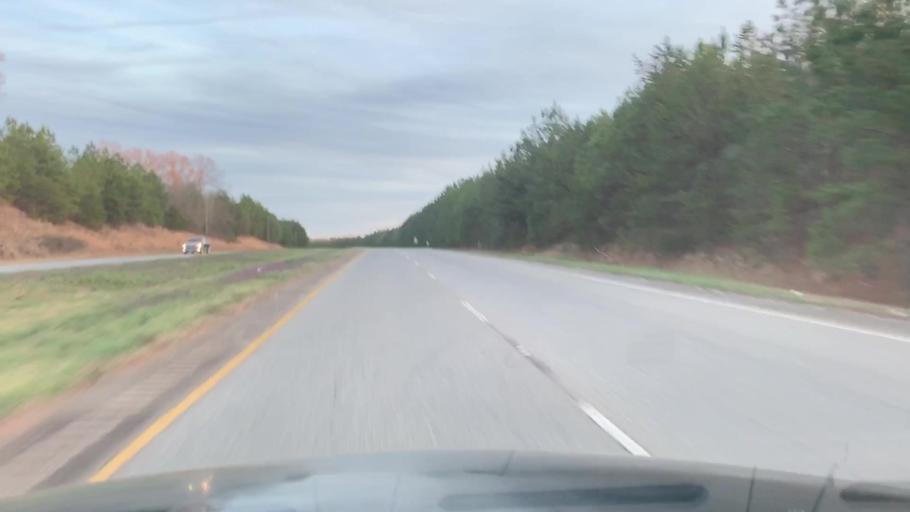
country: US
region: South Carolina
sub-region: Greenville County
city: Golden Grove
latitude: 34.7355
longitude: -82.4291
